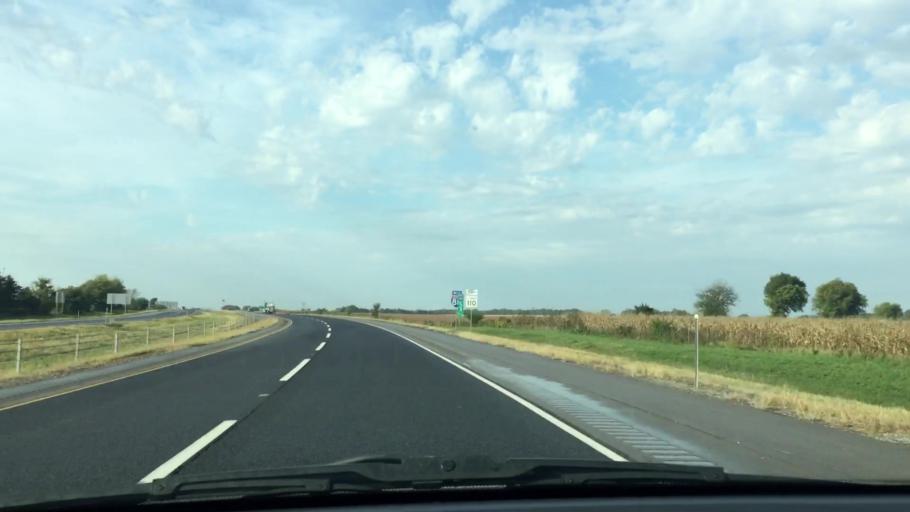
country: US
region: Illinois
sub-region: Lee County
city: Dixon
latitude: 41.8165
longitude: -89.4804
